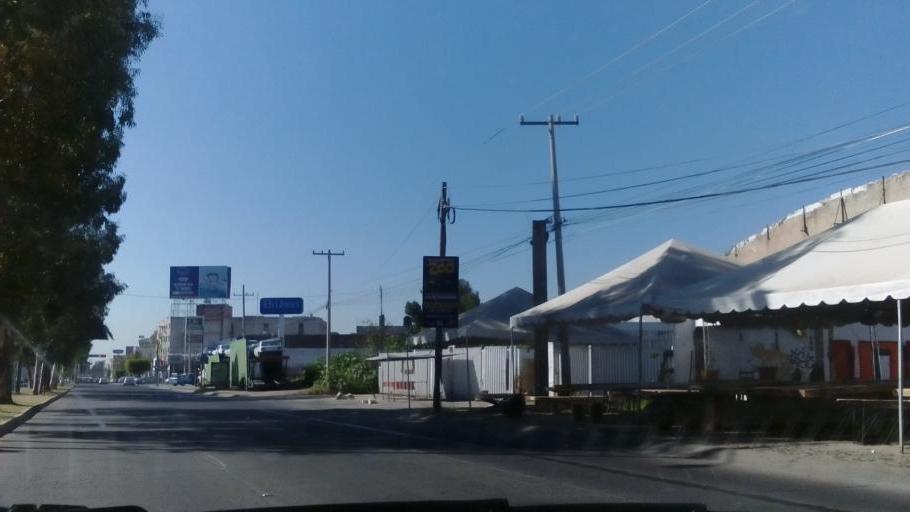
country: MX
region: Guanajuato
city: Leon
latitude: 21.1521
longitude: -101.6847
